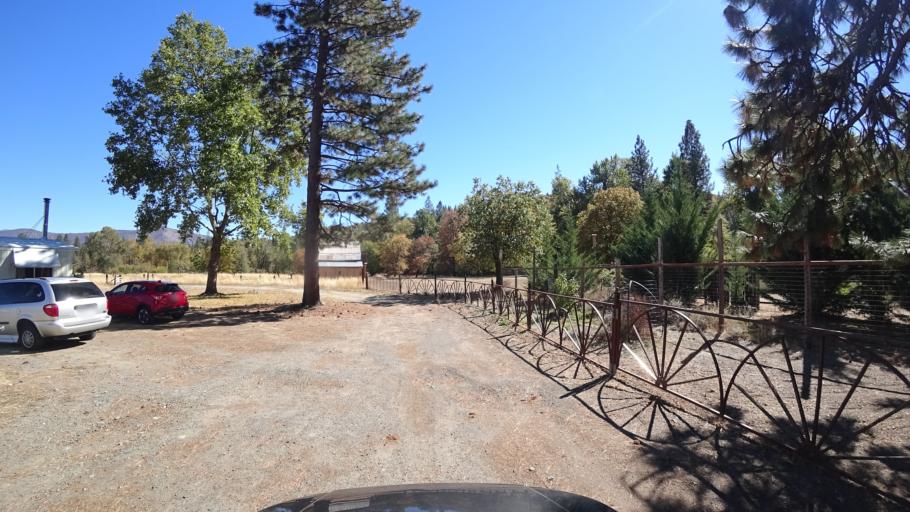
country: US
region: California
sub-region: Siskiyou County
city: Yreka
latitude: 41.4540
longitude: -122.8857
